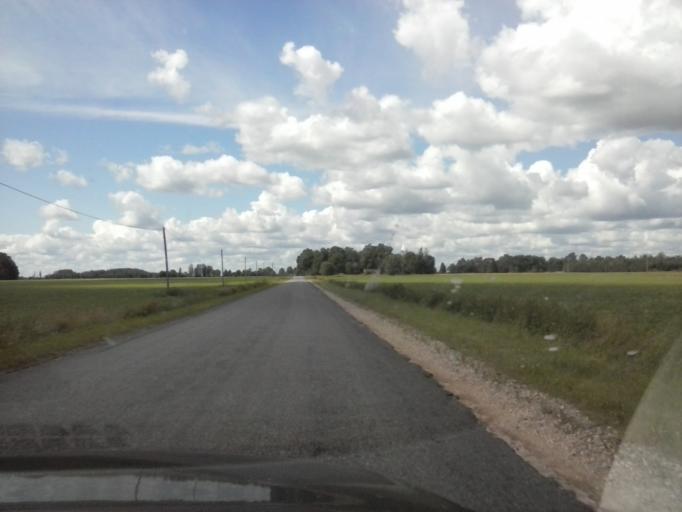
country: EE
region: Laeaene-Virumaa
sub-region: Rakke vald
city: Rakke
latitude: 59.0522
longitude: 26.3626
